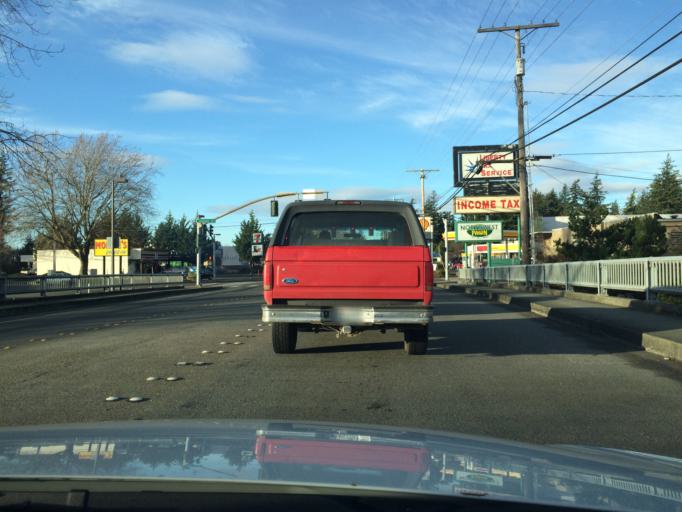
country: US
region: Washington
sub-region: Whatcom County
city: Bellingham
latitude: 48.7734
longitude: -122.4954
